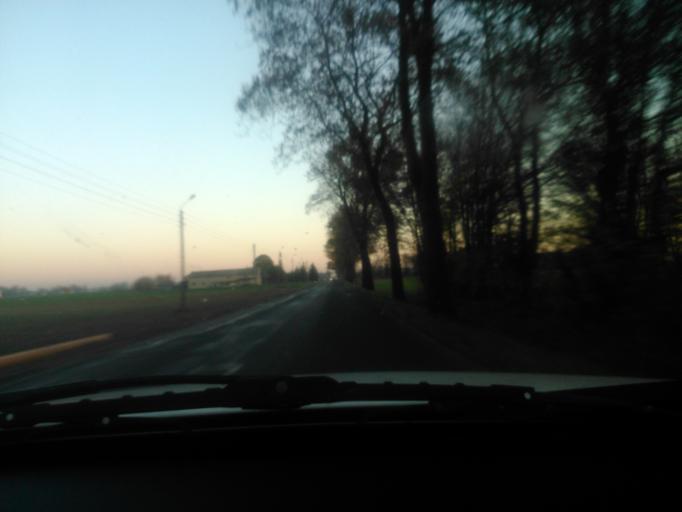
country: PL
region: Kujawsko-Pomorskie
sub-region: Powiat golubsko-dobrzynski
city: Golub-Dobrzyn
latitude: 53.1278
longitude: 19.0272
